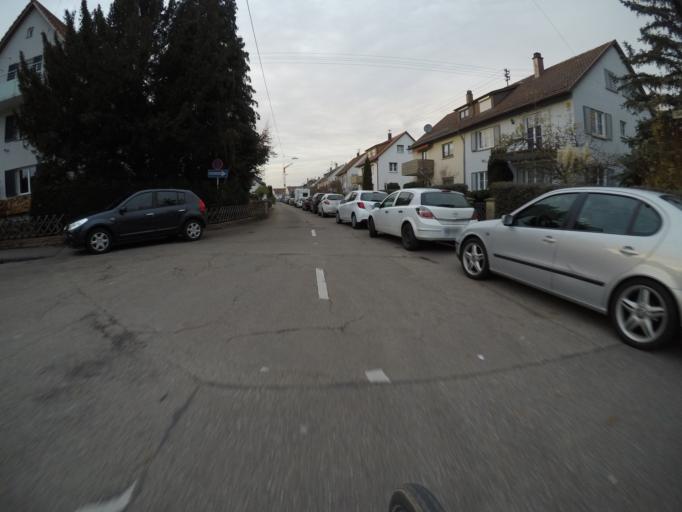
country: DE
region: Baden-Wuerttemberg
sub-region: Regierungsbezirk Stuttgart
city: Ostfildern
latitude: 48.7312
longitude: 9.2590
